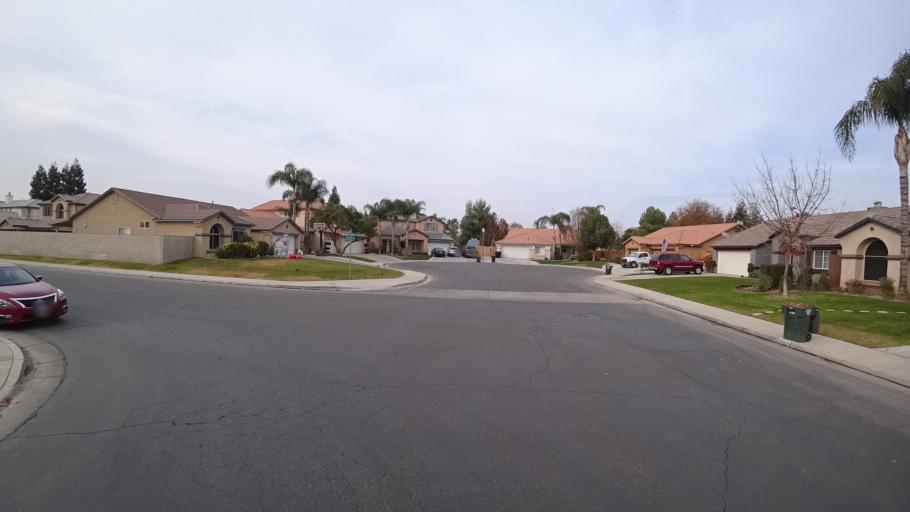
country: US
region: California
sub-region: Kern County
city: Rosedale
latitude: 35.3451
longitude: -119.1331
